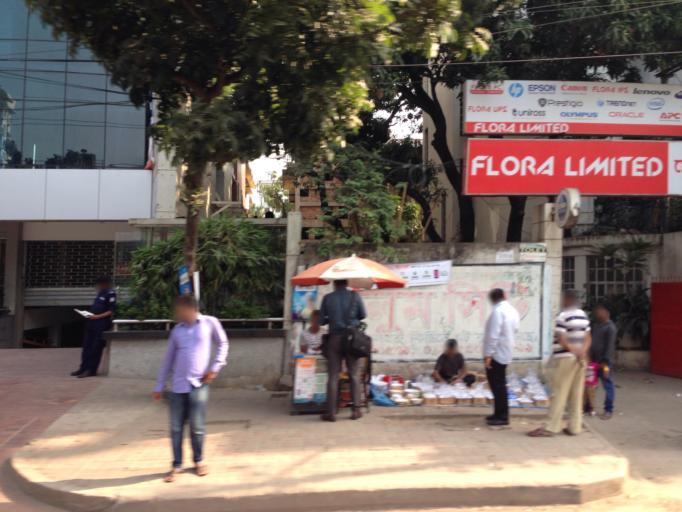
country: BD
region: Dhaka
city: Azimpur
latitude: 23.7425
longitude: 90.3828
